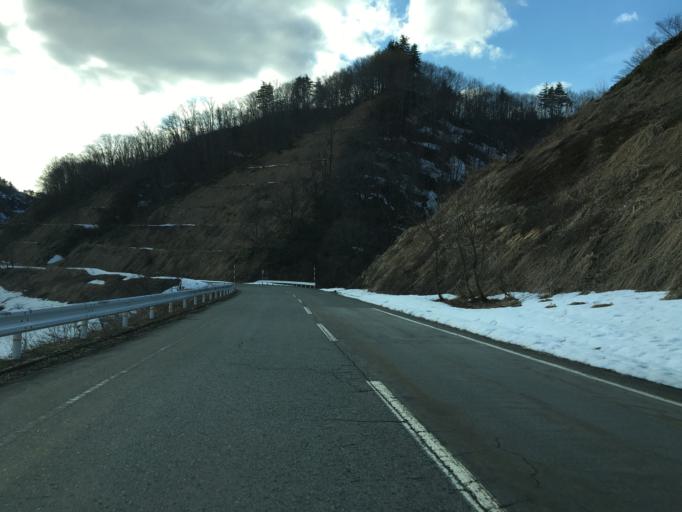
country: JP
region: Yamagata
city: Yonezawa
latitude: 37.9228
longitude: 139.9327
